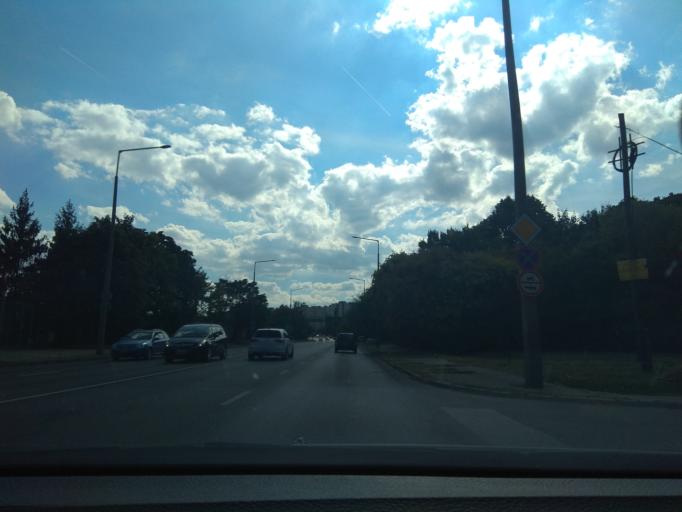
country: HU
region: Borsod-Abauj-Zemplen
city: Miskolc
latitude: 48.0864
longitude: 20.7901
